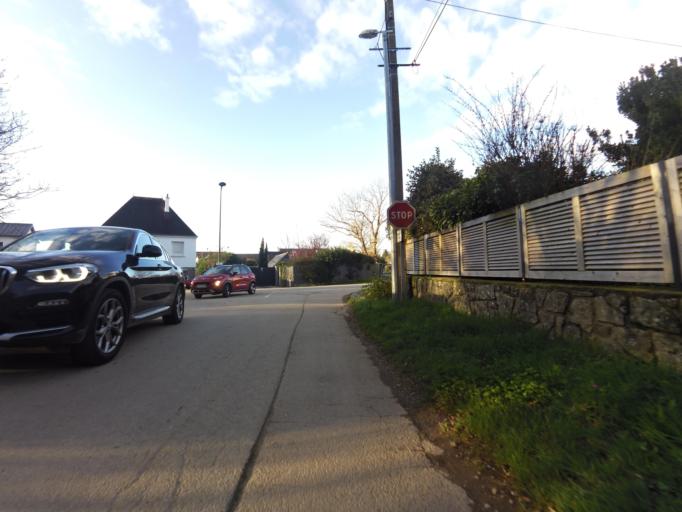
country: FR
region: Brittany
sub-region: Departement du Morbihan
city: Arradon
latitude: 47.6343
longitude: -2.8146
